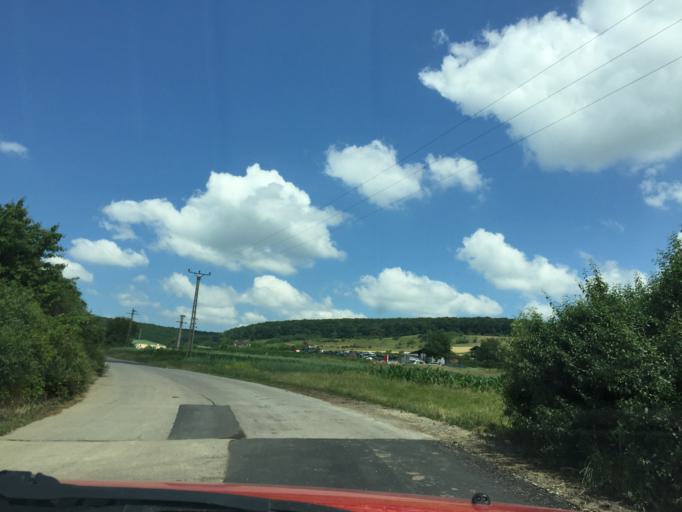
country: RO
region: Cluj
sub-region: Comuna Baciu
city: Baciu
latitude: 46.7989
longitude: 23.5583
